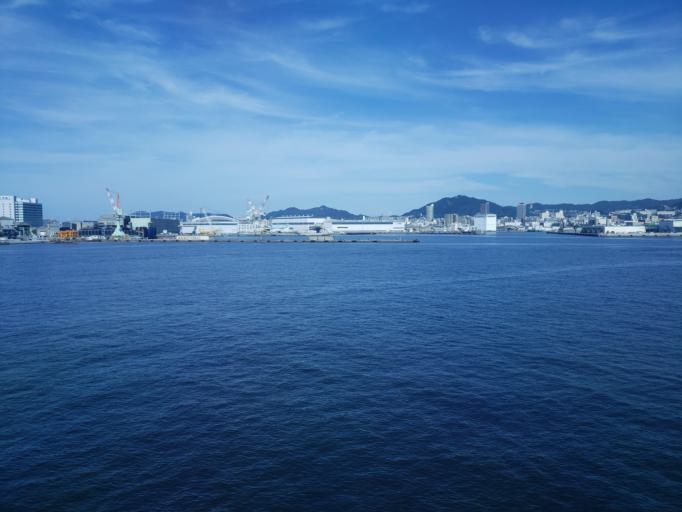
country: JP
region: Hyogo
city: Kobe
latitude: 34.6581
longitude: 135.1891
